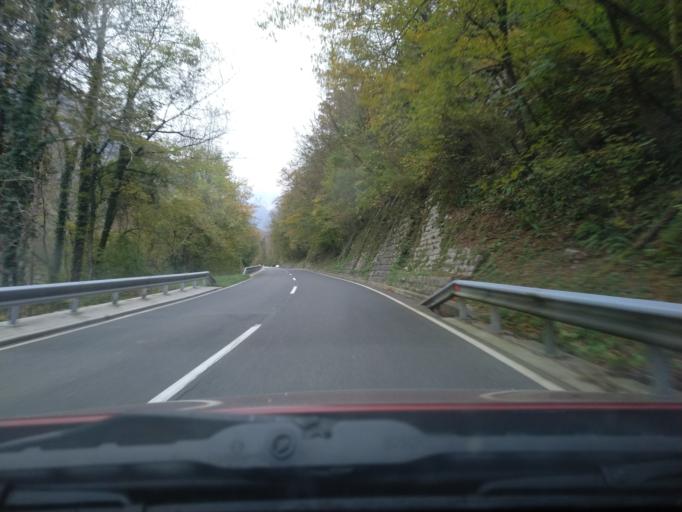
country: SI
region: Kobarid
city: Kobarid
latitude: 46.2765
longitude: 13.5585
